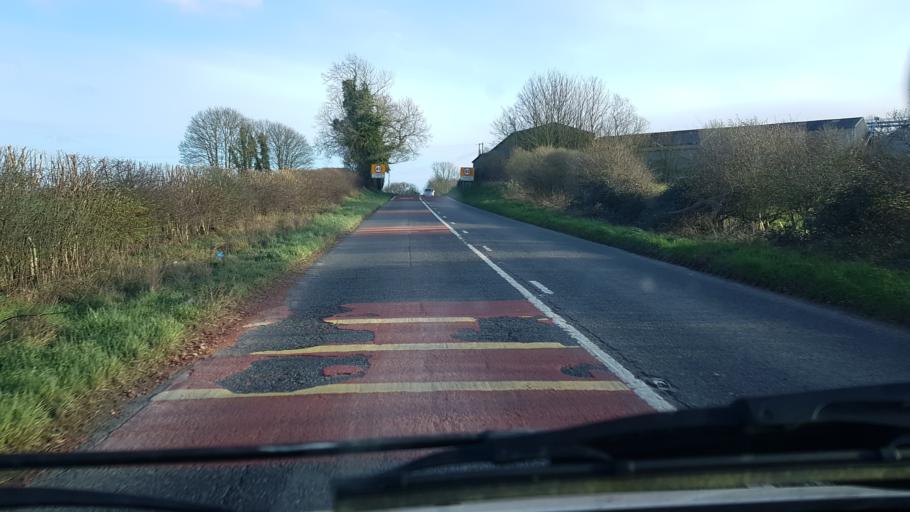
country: GB
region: England
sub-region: Wiltshire
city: Collingbourne Kingston
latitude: 51.3119
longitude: -1.6639
